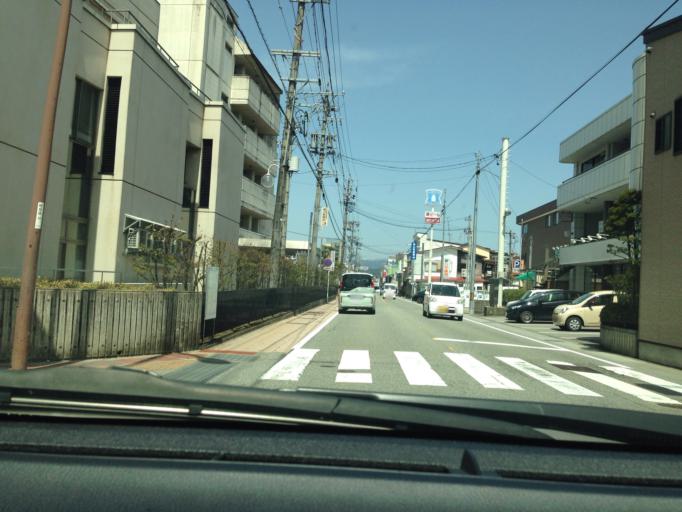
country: JP
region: Gifu
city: Takayama
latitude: 36.1362
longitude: 137.2552
